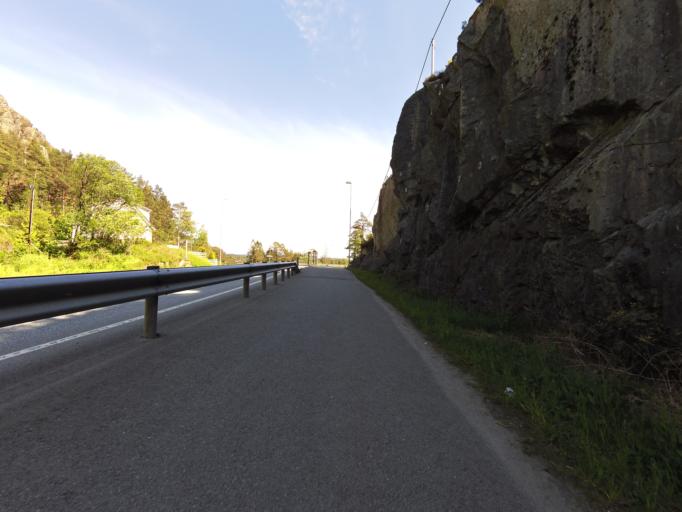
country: NO
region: Hordaland
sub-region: Stord
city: Sagvag
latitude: 59.7824
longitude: 5.3776
